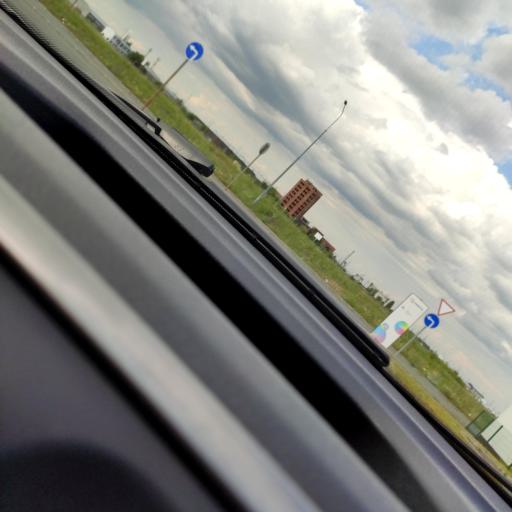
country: RU
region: Samara
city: Tol'yatti
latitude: 53.5518
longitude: 49.3440
